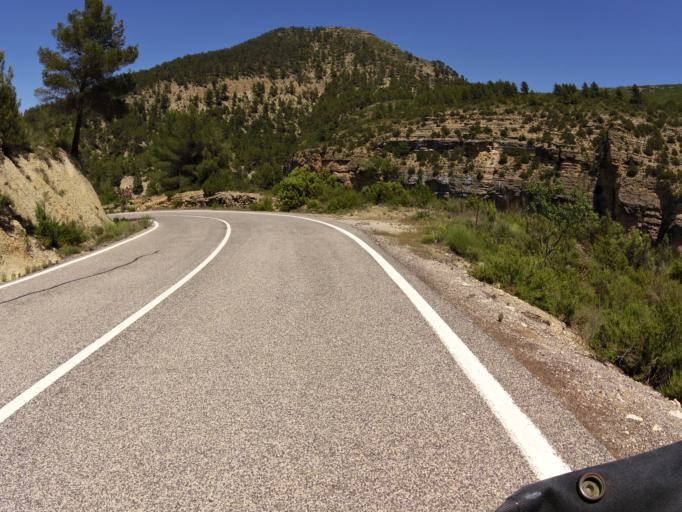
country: ES
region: Valencia
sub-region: Provincia de Valencia
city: Casas Bajas
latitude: 39.9866
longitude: -1.2751
